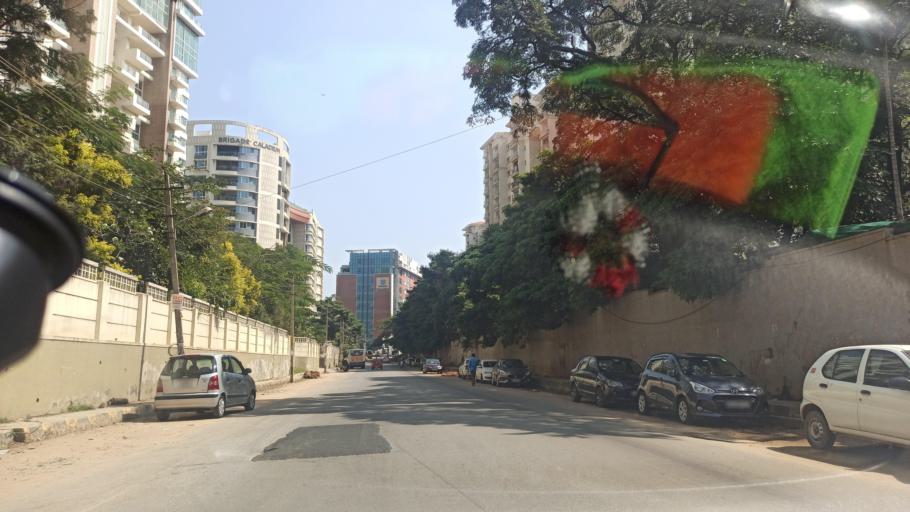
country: IN
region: Karnataka
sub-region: Bangalore Urban
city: Yelahanka
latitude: 13.0557
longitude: 77.5948
